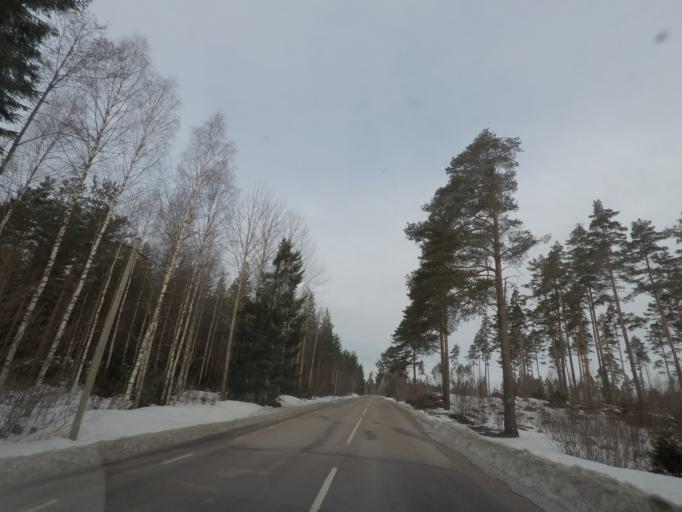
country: SE
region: Vaestmanland
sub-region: Vasteras
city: Skultuna
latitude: 59.7526
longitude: 16.3207
